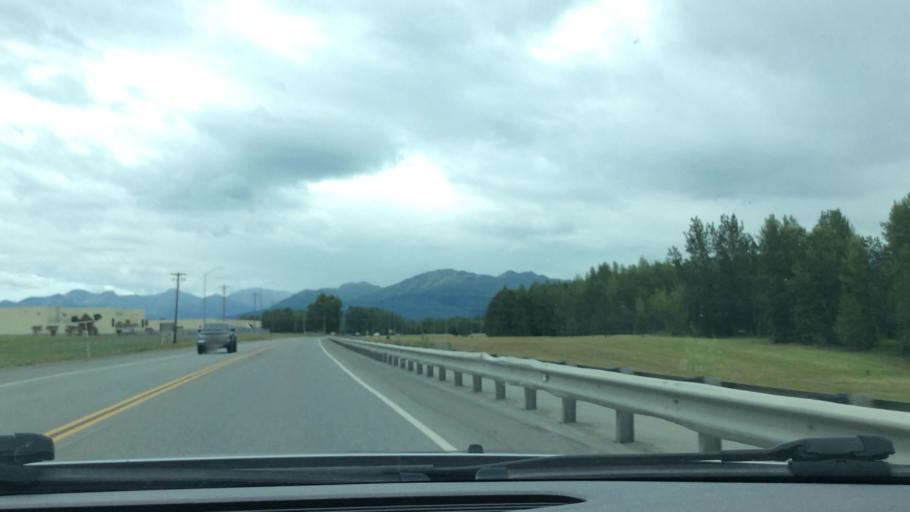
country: US
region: Alaska
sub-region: Anchorage Municipality
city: Anchorage
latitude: 61.2396
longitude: -149.7906
